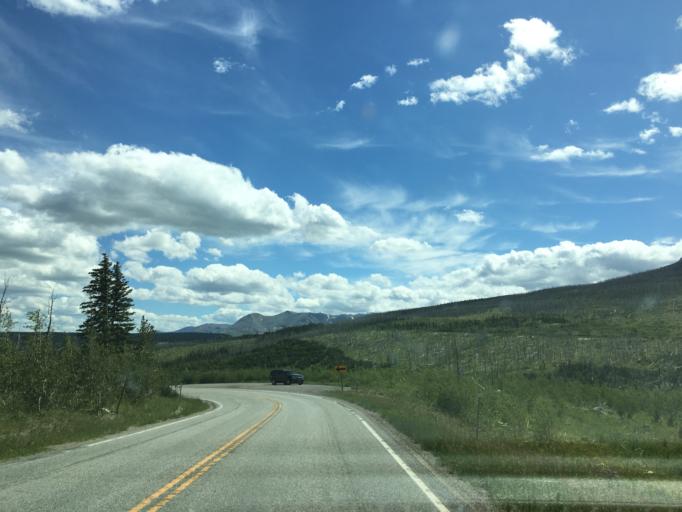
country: US
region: Montana
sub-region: Glacier County
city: North Browning
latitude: 48.6812
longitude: -113.3571
